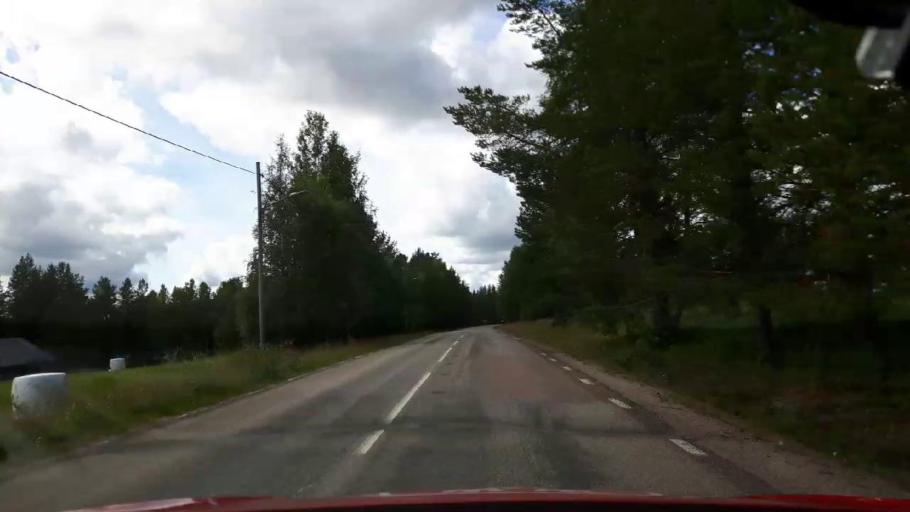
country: SE
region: Jaemtland
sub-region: Harjedalens Kommun
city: Sveg
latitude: 61.8452
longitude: 14.0479
